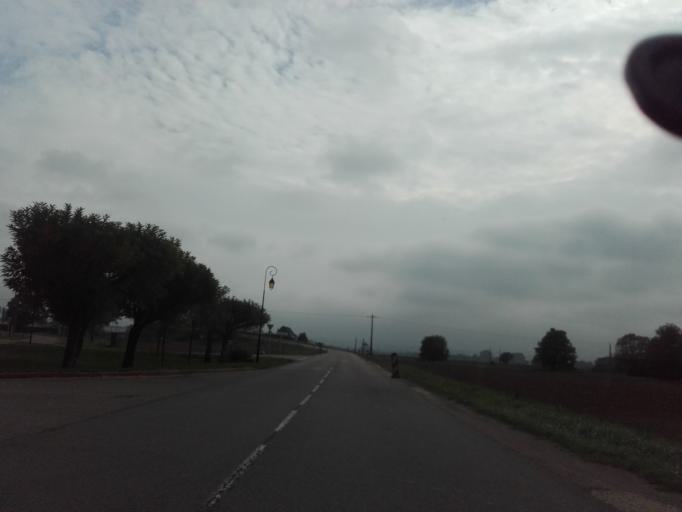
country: FR
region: Bourgogne
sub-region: Departement de la Cote-d'Or
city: Meursault
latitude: 46.9695
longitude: 4.7898
